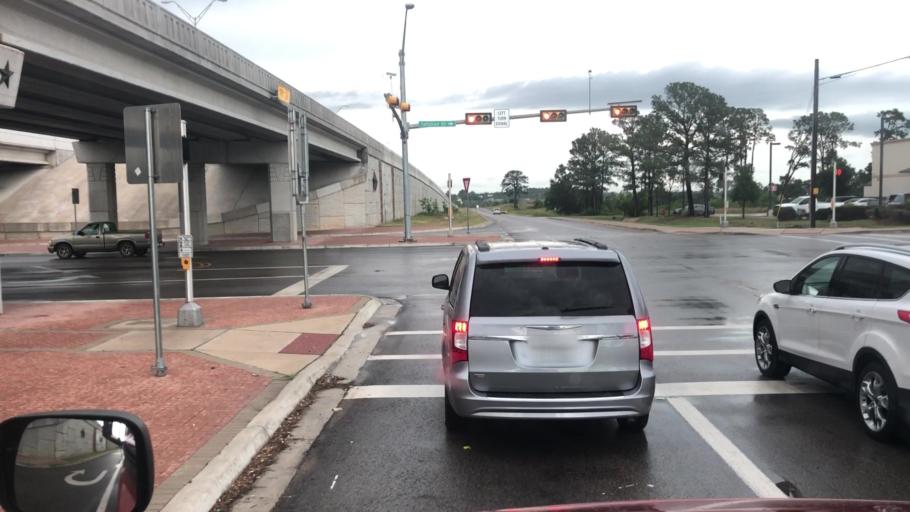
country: US
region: Texas
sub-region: Bastrop County
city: Bastrop
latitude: 30.1023
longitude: -97.2847
